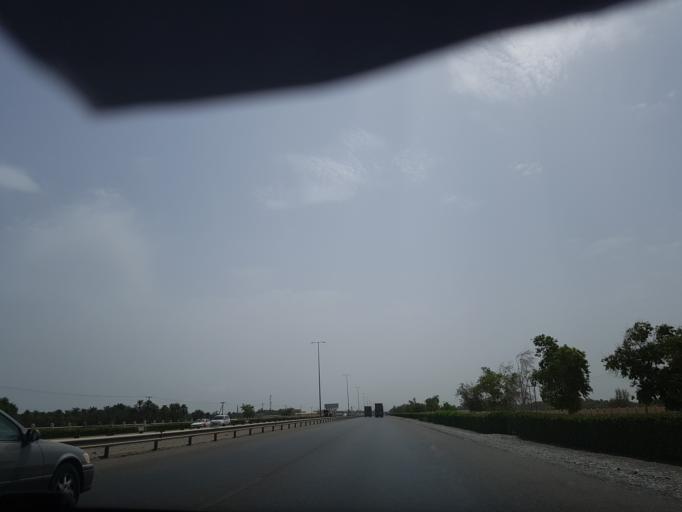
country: OM
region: Al Batinah
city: Barka'
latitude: 23.7360
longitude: 57.6666
